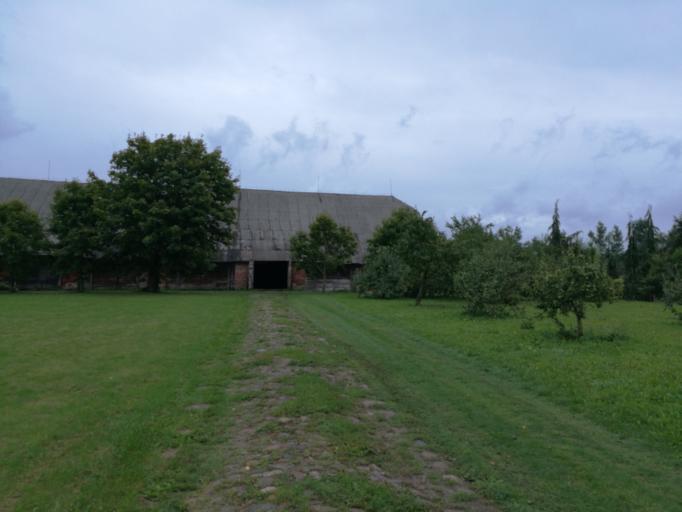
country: LT
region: Kauno apskritis
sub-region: Kaunas
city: Sargenai
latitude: 55.0645
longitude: 23.7920
